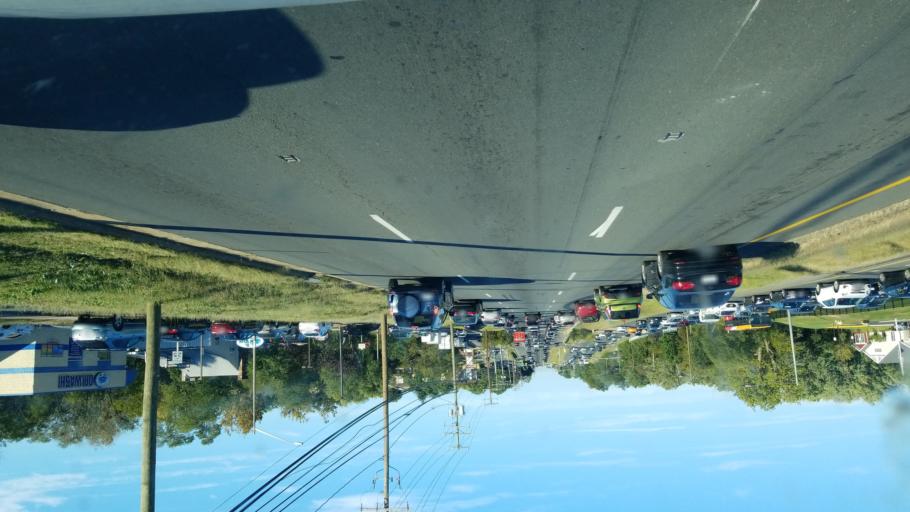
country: US
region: Virginia
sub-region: Fairfax County
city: Chantilly
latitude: 38.8902
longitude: -77.4215
